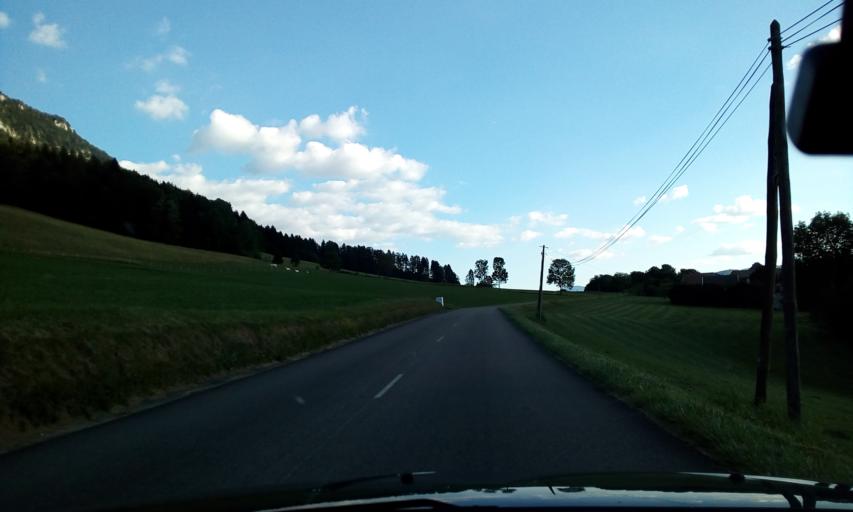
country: FR
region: Rhone-Alpes
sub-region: Departement de l'Isere
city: Meaudre
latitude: 45.0686
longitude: 5.4588
